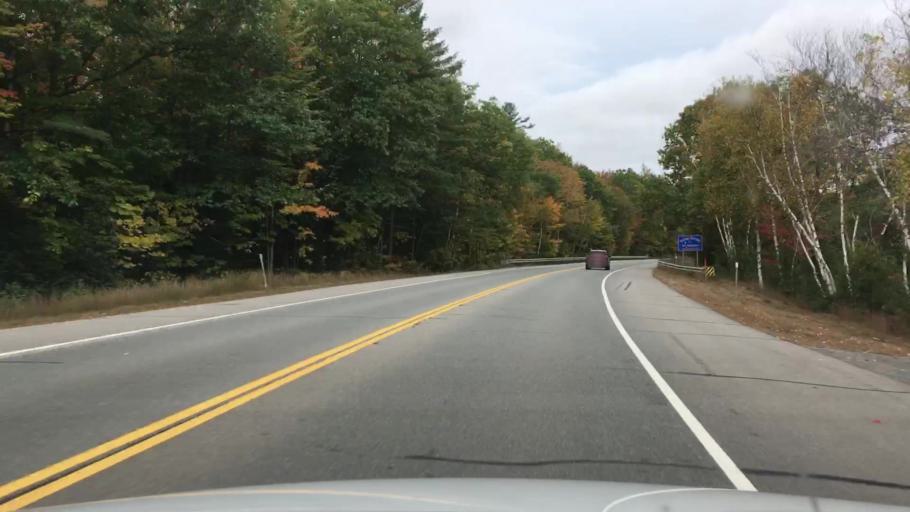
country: US
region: New Hampshire
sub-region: Coos County
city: Gorham
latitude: 44.3849
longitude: -71.0224
